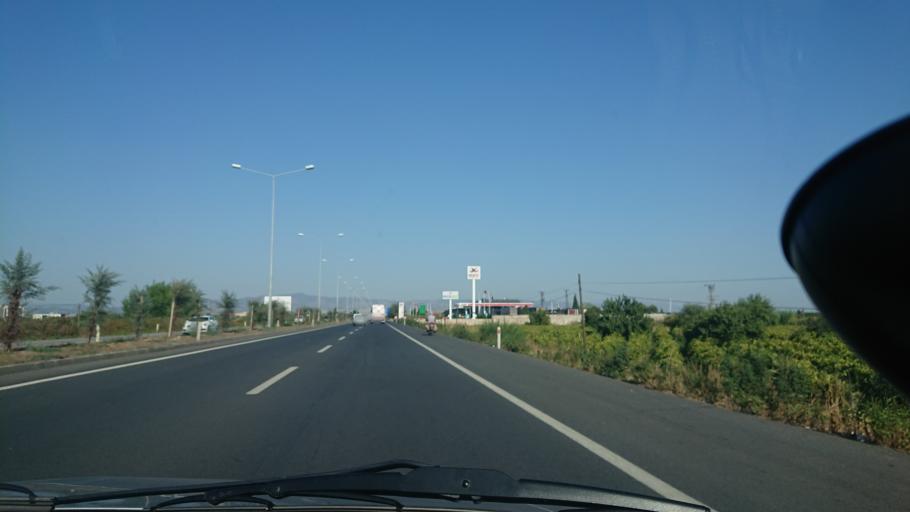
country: TR
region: Manisa
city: Salihli
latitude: 38.4965
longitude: 28.1887
